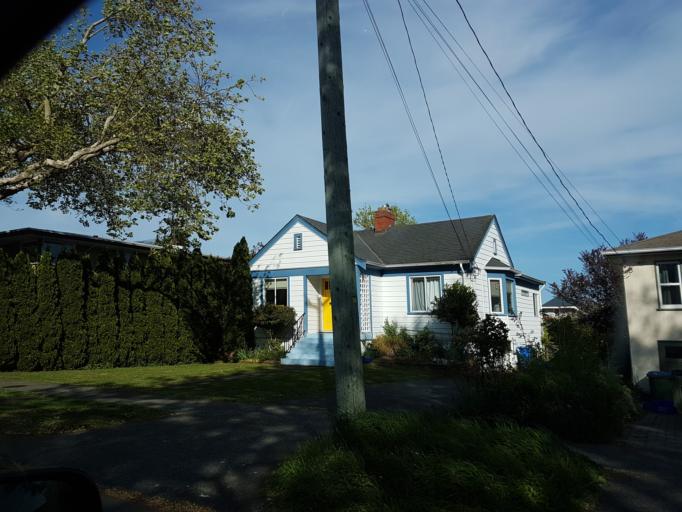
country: CA
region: British Columbia
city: Oak Bay
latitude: 48.4354
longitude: -123.3043
